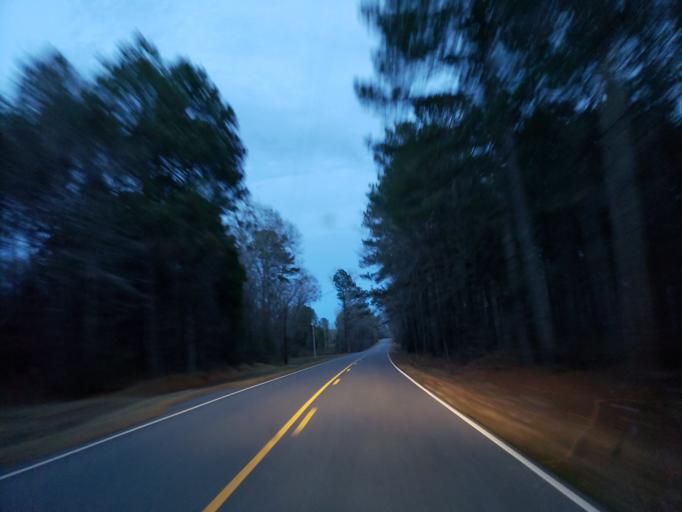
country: US
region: Alabama
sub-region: Greene County
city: Eutaw
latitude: 32.8848
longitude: -88.0568
